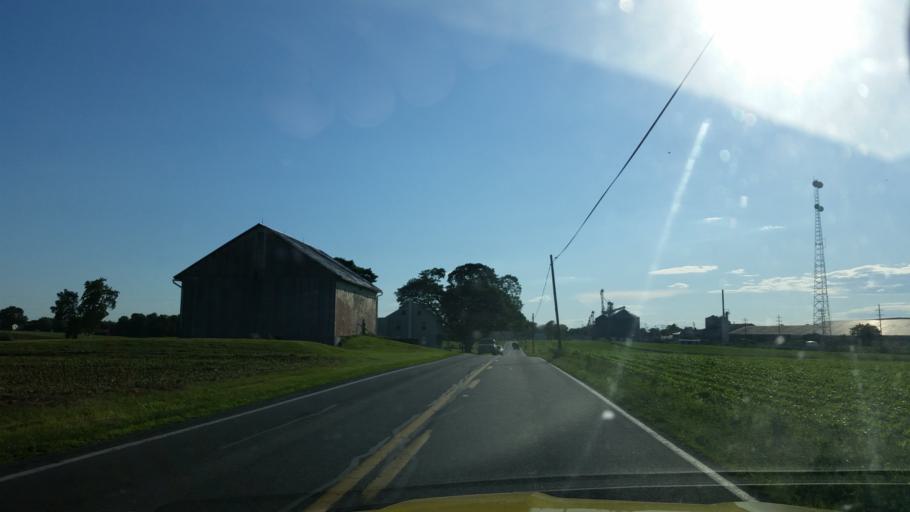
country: US
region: Pennsylvania
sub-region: Lebanon County
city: Avon
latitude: 40.3475
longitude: -76.3754
